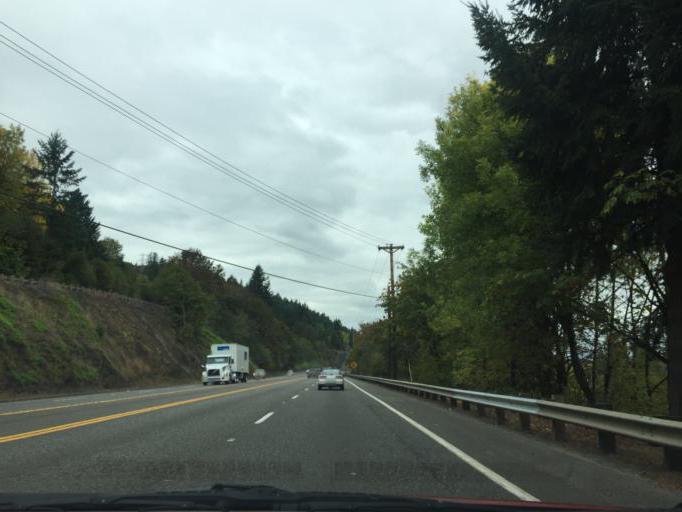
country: US
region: Oregon
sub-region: Washington County
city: Oak Hills
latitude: 45.6182
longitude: -122.8072
